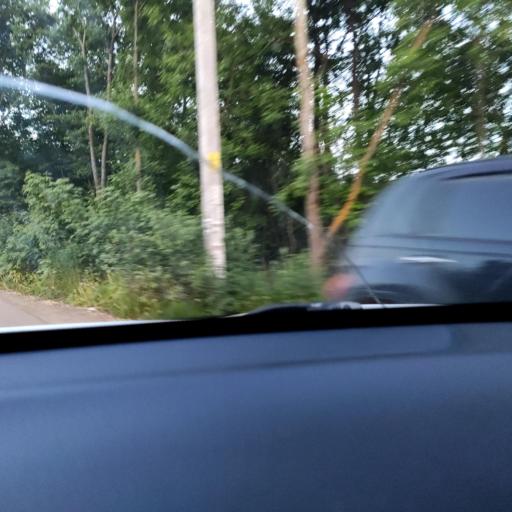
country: RU
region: Tatarstan
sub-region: Gorod Kazan'
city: Kazan
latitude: 55.8476
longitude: 49.1672
